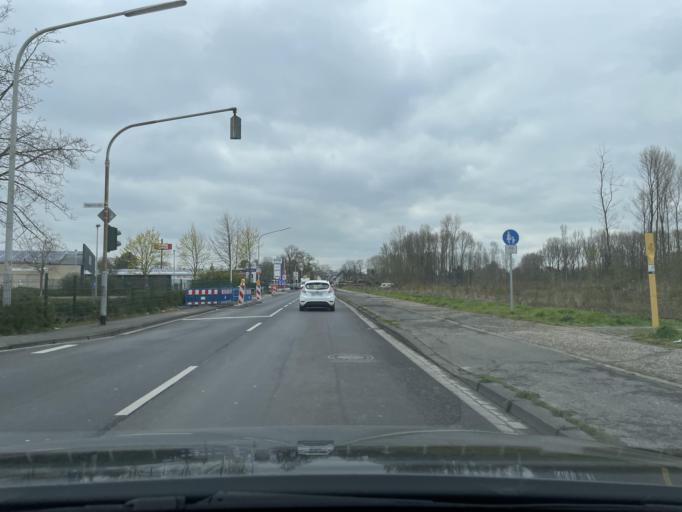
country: DE
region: North Rhine-Westphalia
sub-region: Regierungsbezirk Dusseldorf
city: Monchengladbach
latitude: 51.1628
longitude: 6.4599
